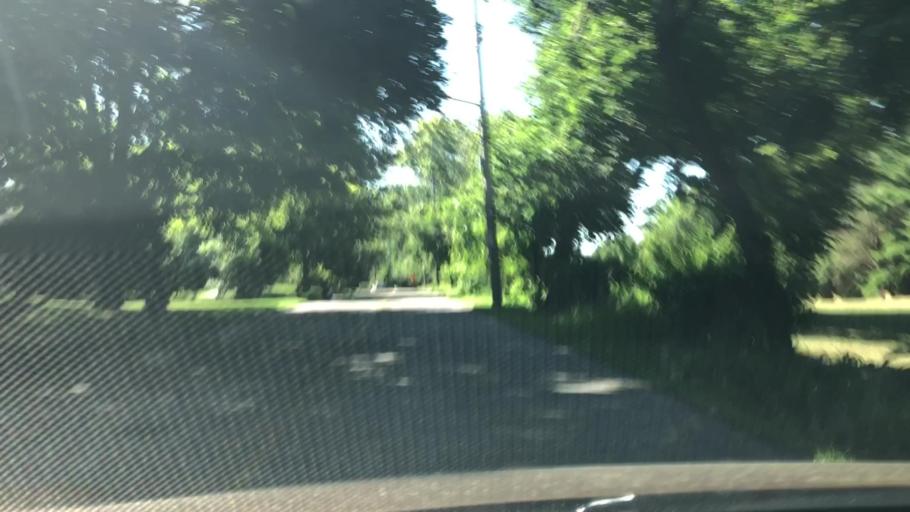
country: US
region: New York
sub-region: Westchester County
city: White Plains
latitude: 41.0193
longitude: -73.7472
